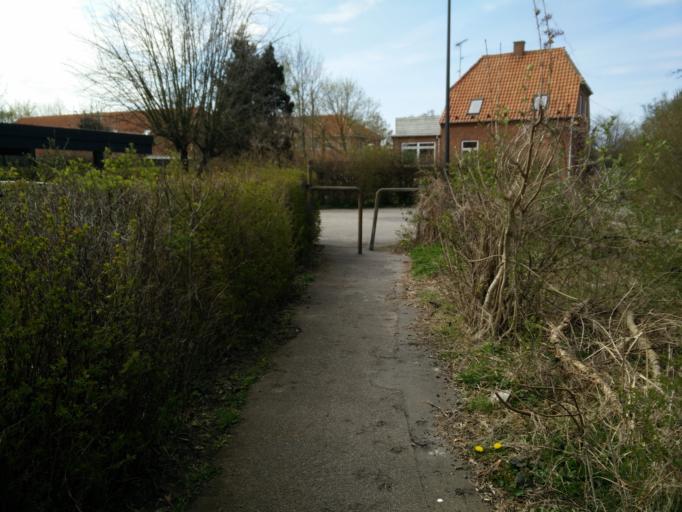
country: DK
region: Capital Region
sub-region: Herlev Kommune
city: Herlev
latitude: 55.7226
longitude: 12.4462
